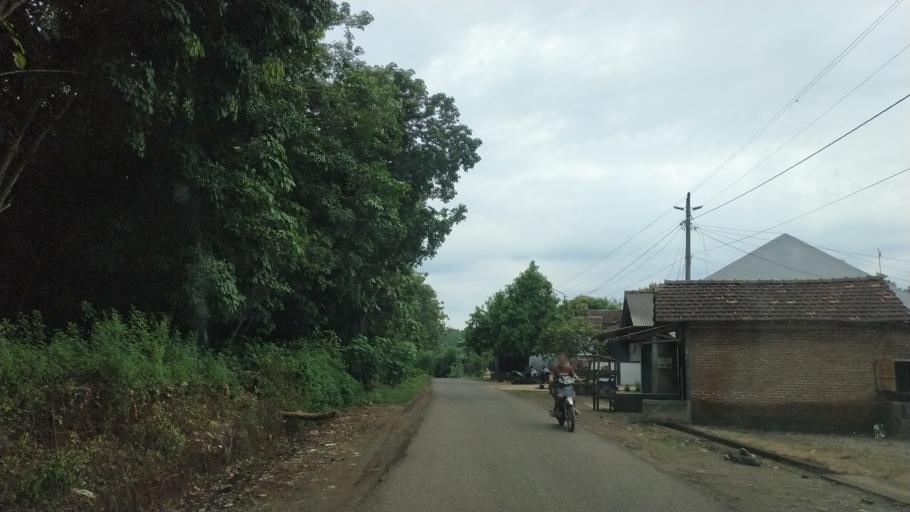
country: ID
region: Central Java
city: Krajan Tegalombo
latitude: -6.4414
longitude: 110.9824
